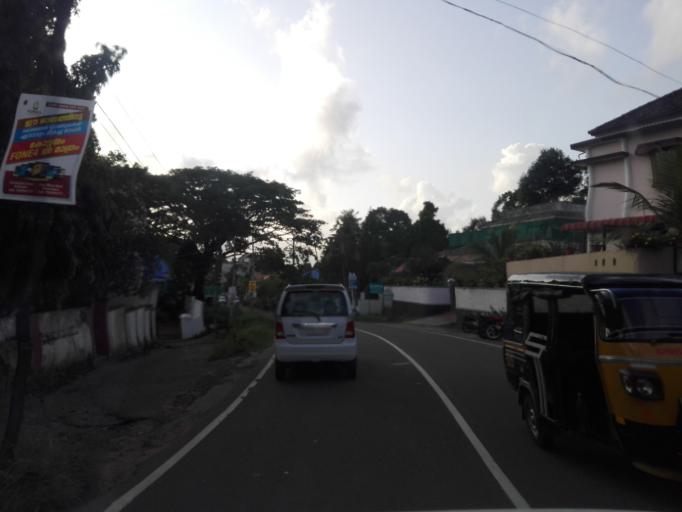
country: IN
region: Kerala
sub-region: Kottayam
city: Kottayam
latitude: 9.5952
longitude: 76.5137
